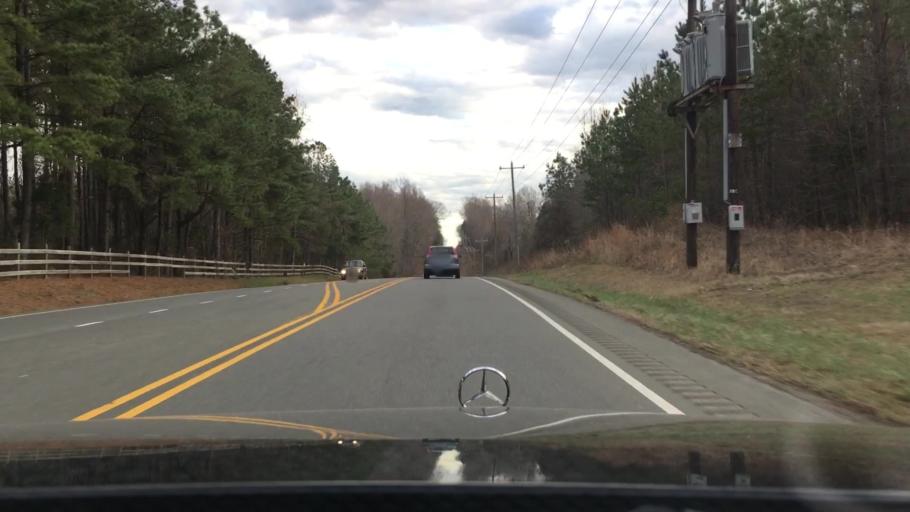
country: US
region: North Carolina
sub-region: Orange County
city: Hillsborough
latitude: 36.1085
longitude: -79.1104
